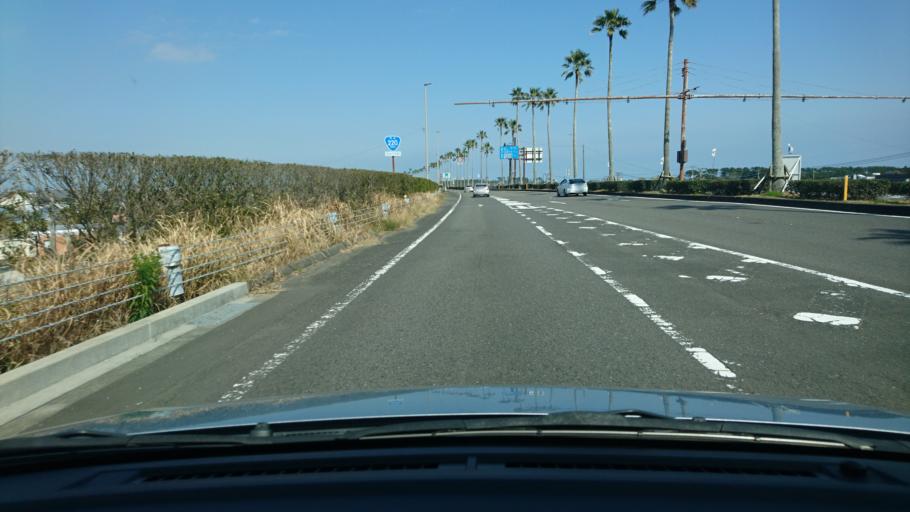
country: JP
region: Miyazaki
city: Miyazaki-shi
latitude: 31.8309
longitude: 131.4430
